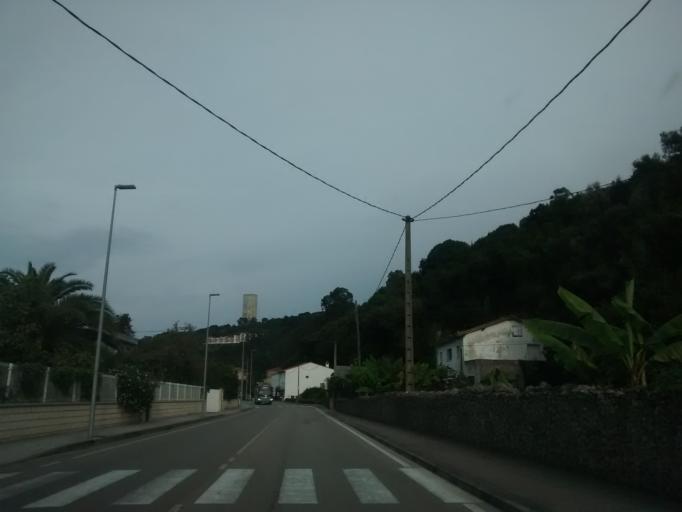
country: ES
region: Cantabria
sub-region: Provincia de Cantabria
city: Laredo
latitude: 43.4039
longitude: -3.4212
